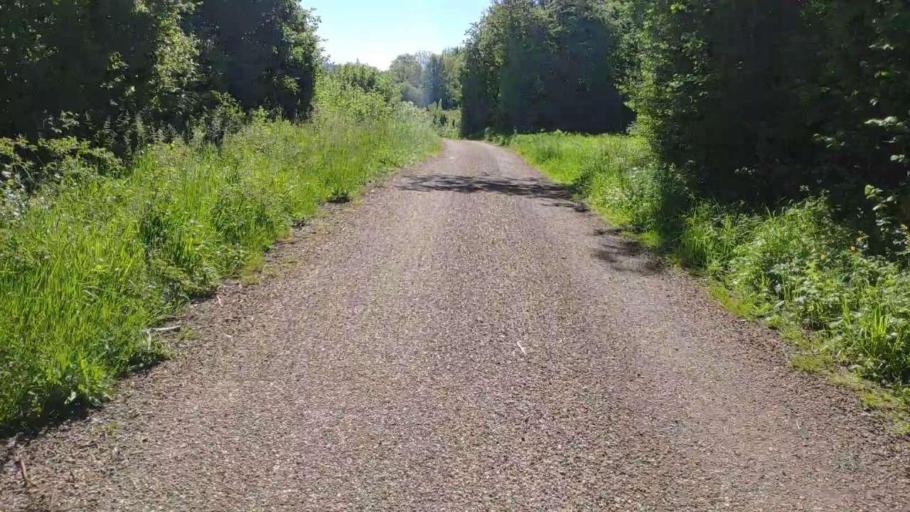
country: FR
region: Franche-Comte
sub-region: Departement du Jura
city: Perrigny
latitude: 46.6857
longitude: 5.6697
